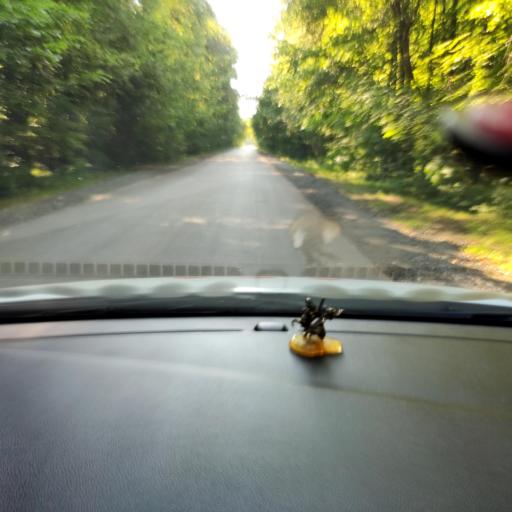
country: RU
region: Tatarstan
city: Stolbishchi
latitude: 55.7013
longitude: 49.2182
